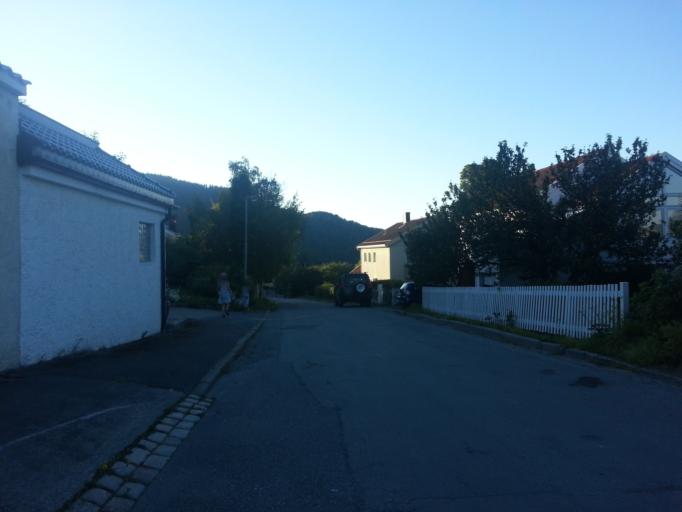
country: NO
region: Sor-Trondelag
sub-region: Trondheim
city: Trondheim
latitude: 63.4267
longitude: 10.3633
